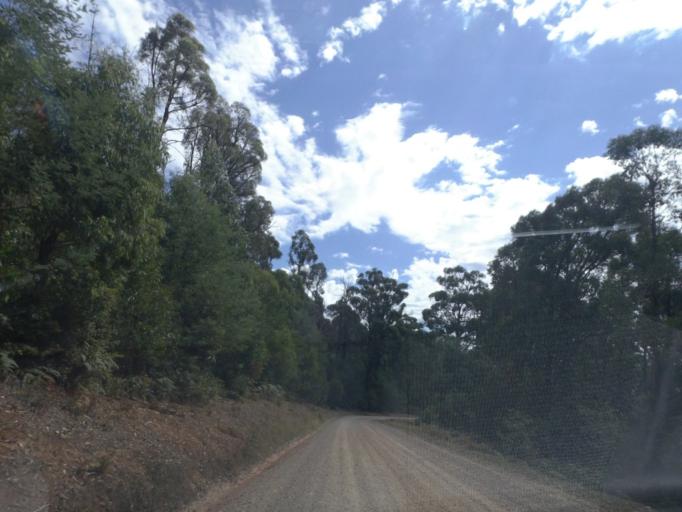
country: AU
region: Victoria
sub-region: Murrindindi
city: Alexandra
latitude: -37.4636
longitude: 145.7807
